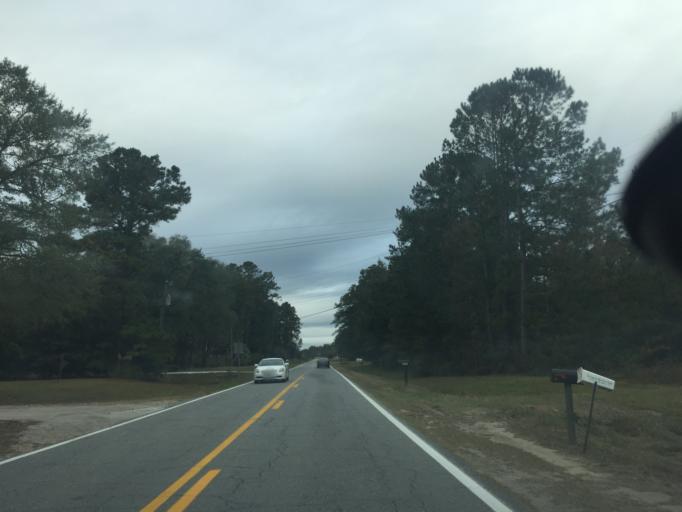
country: US
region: Georgia
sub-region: Chatham County
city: Bloomingdale
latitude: 32.0836
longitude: -81.3722
